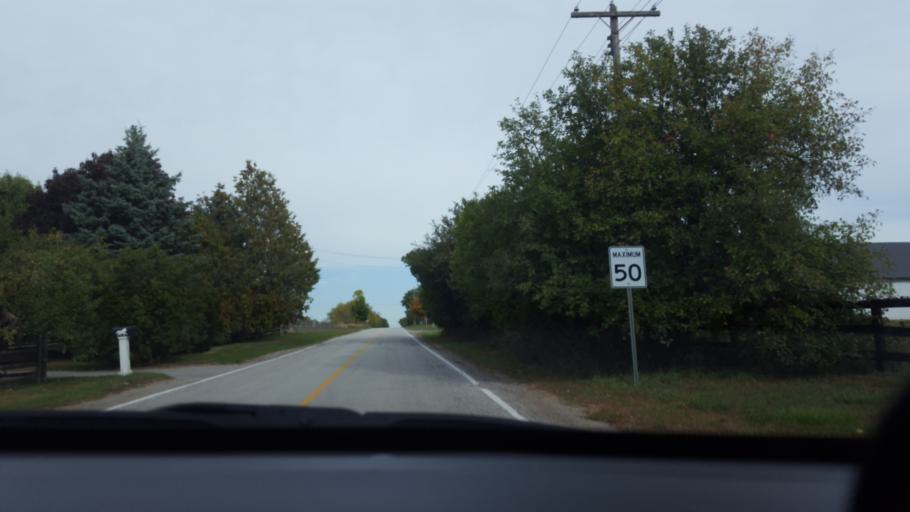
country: CA
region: Ontario
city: Newmarket
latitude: 44.0145
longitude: -79.5507
